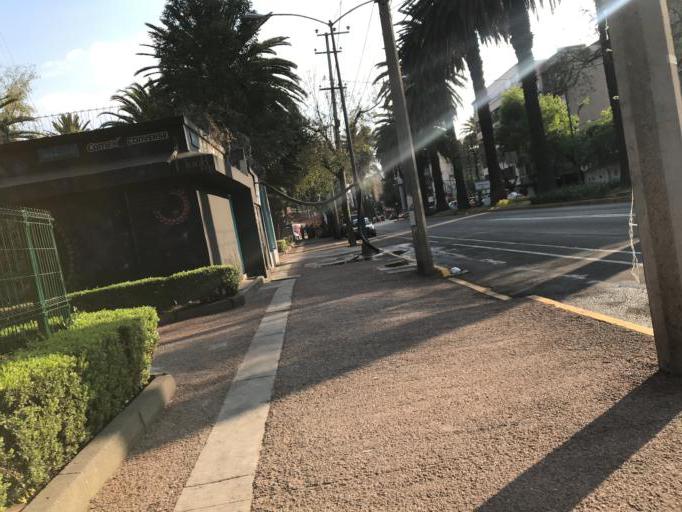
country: MX
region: Mexico City
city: Benito Juarez
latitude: 19.4000
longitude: -99.1505
